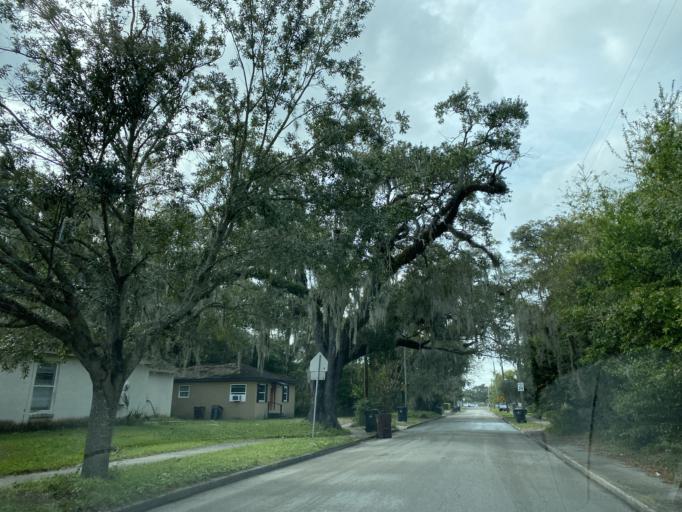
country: US
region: Florida
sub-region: Orange County
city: Orlando
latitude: 28.5476
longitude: -81.3933
